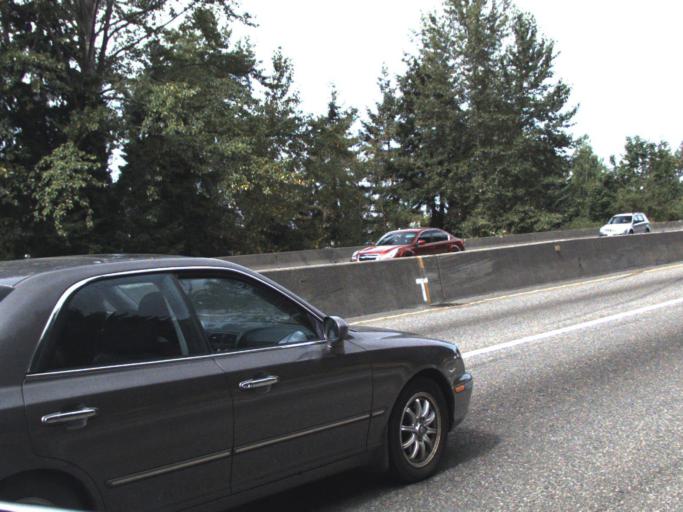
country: US
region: Washington
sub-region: King County
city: Renton
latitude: 47.4944
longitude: -122.1924
